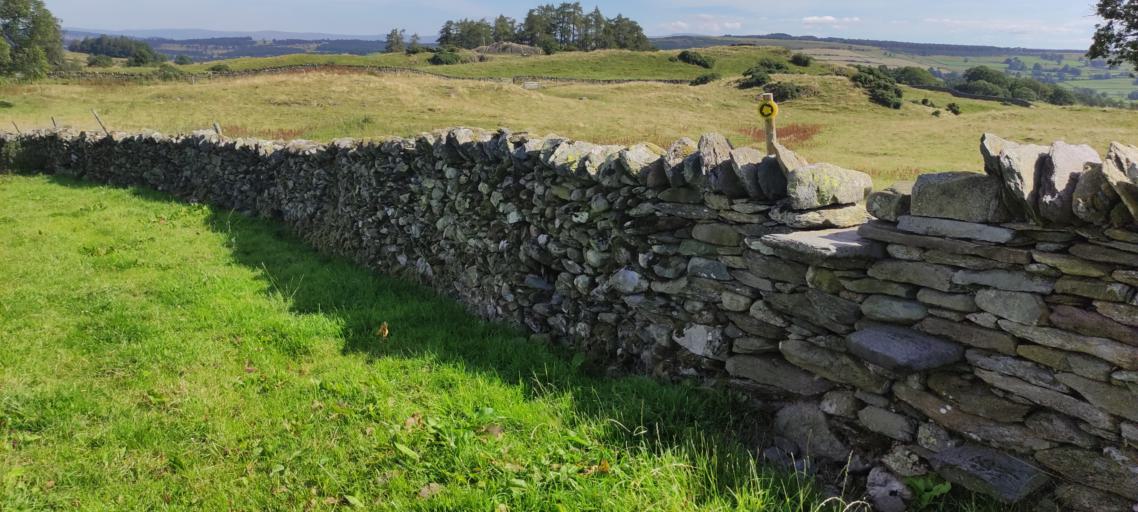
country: GB
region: England
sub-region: Cumbria
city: Penrith
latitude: 54.5475
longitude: -2.7658
